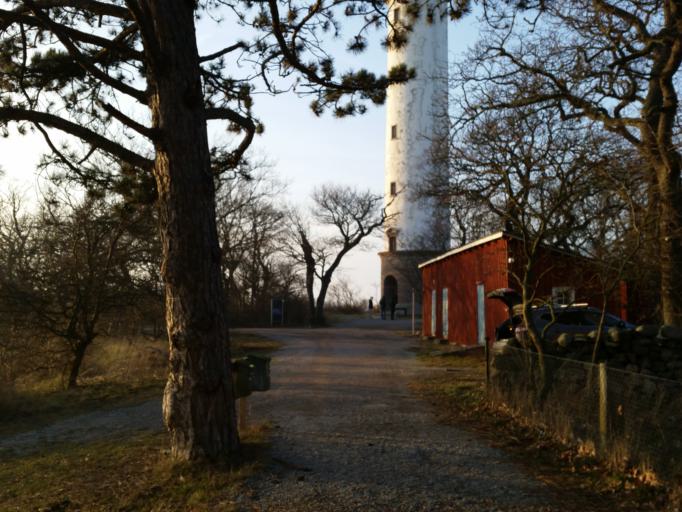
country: SE
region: Kalmar
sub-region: Vasterviks Kommun
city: Vaestervik
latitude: 57.3666
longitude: 17.0974
